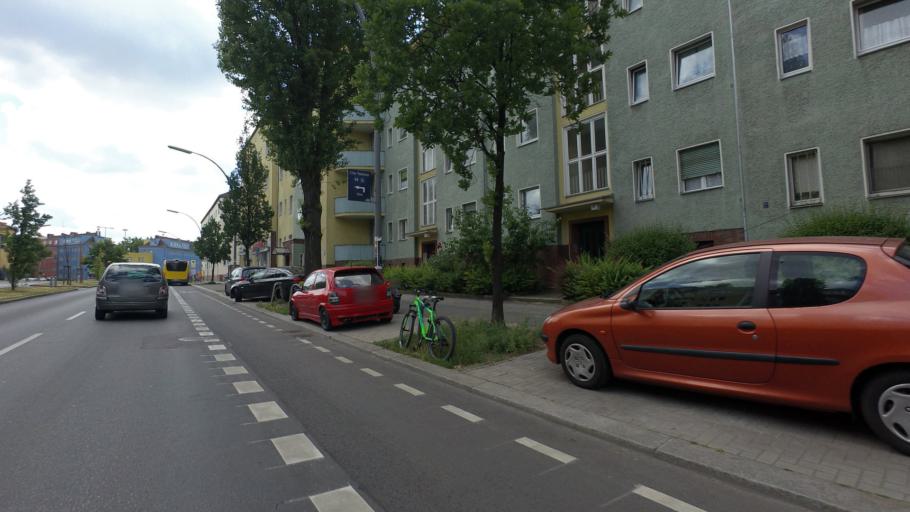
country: DE
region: Berlin
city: Mariendorf
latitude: 52.4568
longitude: 13.3757
